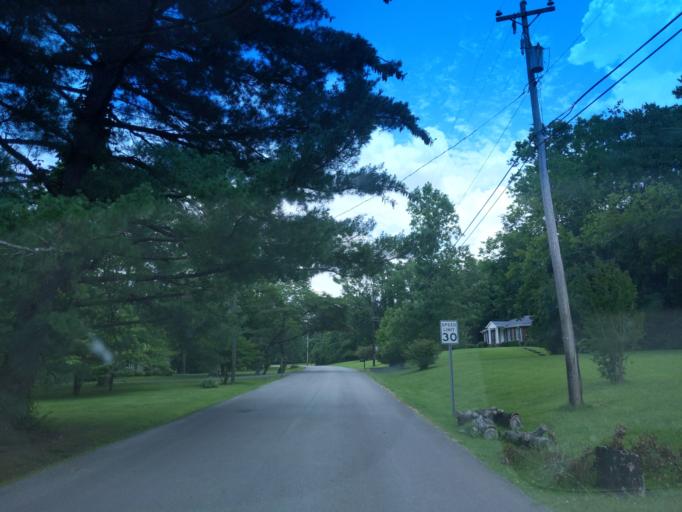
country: US
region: Tennessee
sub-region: Williamson County
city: Brentwood Estates
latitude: 36.0251
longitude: -86.7826
